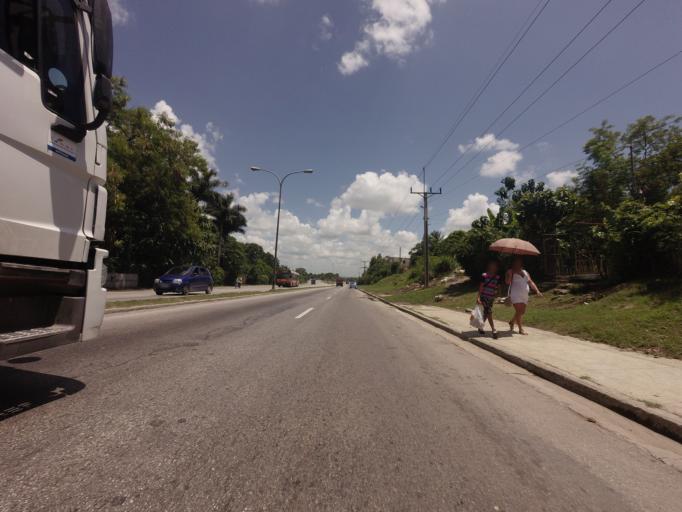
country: CU
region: La Habana
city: Arroyo Naranjo
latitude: 23.0410
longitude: -82.3627
